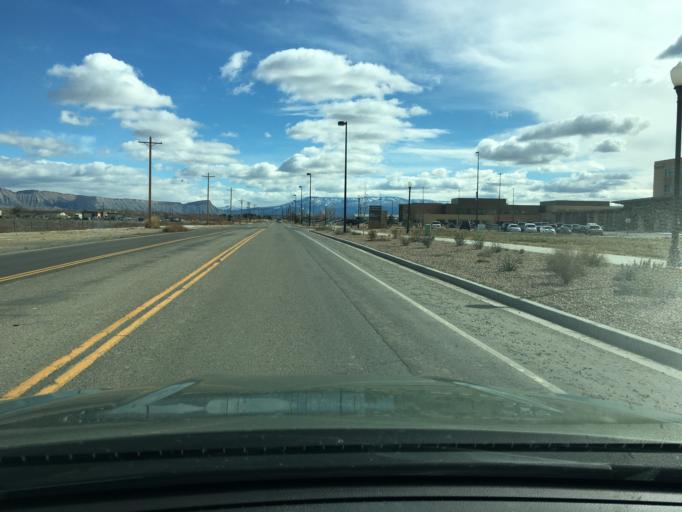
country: US
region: Colorado
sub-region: Mesa County
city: Redlands
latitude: 39.1063
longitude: -108.6168
